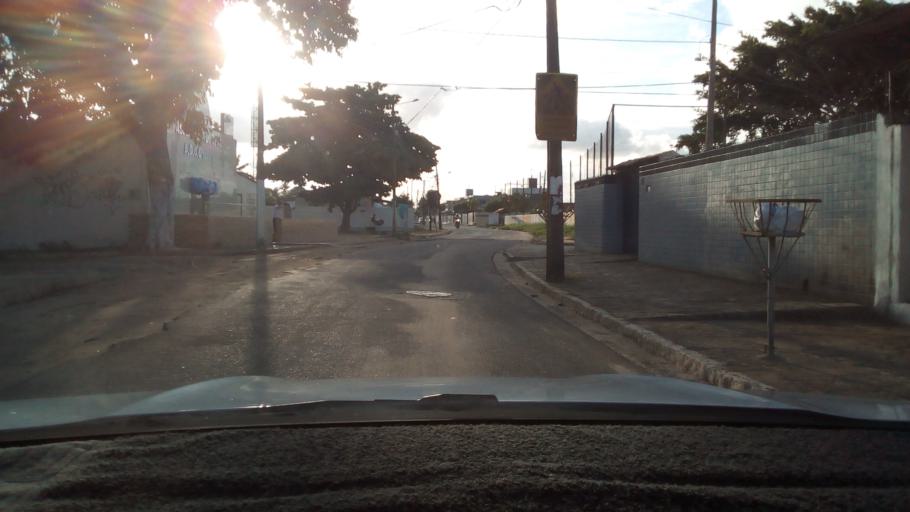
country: BR
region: Paraiba
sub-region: Joao Pessoa
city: Joao Pessoa
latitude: -7.1827
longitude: -34.8706
